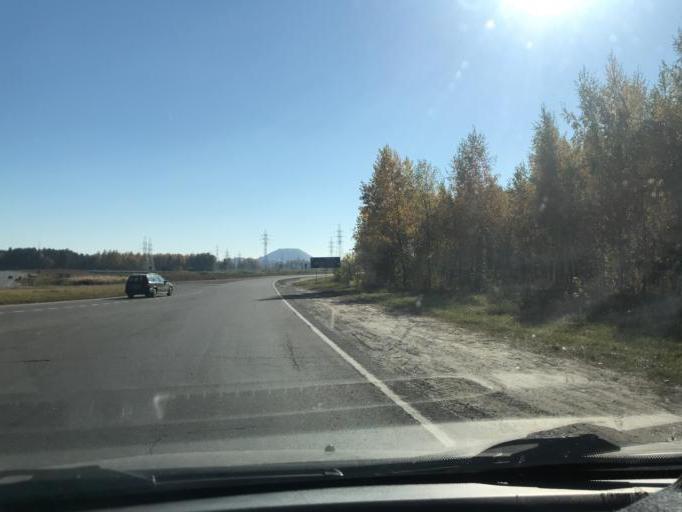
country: BY
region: Gomel
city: Kastsyukowka
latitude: 52.4529
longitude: 30.8239
